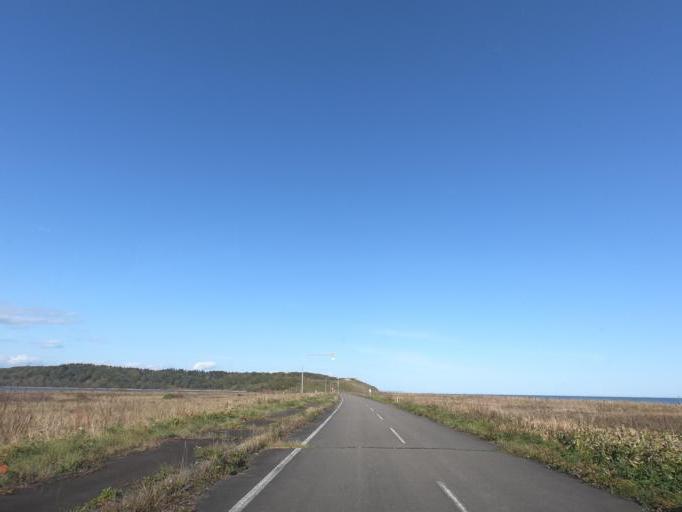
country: JP
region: Hokkaido
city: Obihiro
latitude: 42.5968
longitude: 143.5467
